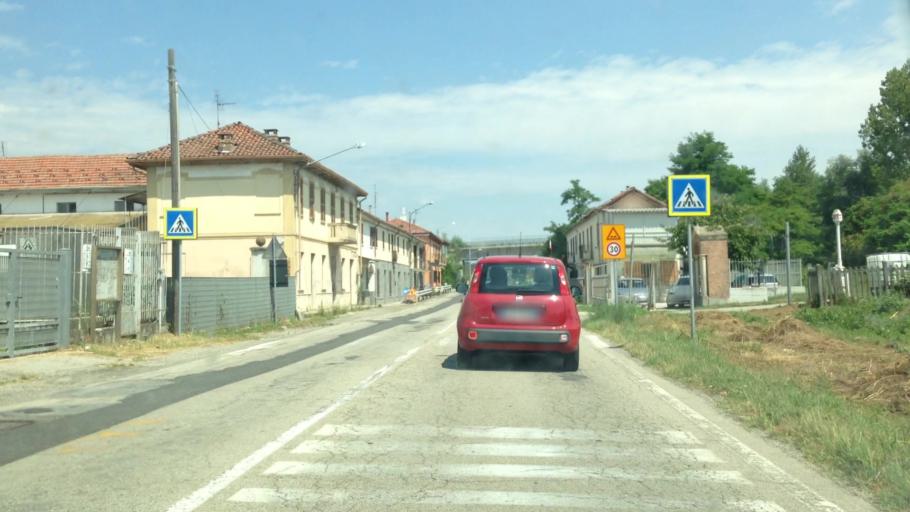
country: IT
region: Piedmont
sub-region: Provincia di Asti
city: Portacomaro
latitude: 44.9432
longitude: 8.2242
